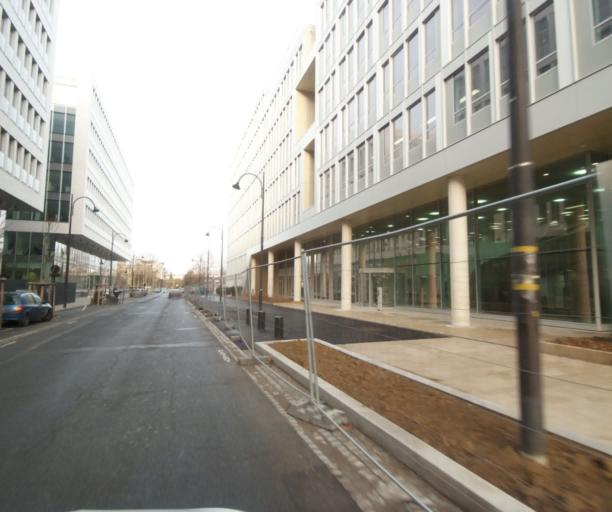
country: FR
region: Ile-de-France
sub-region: Departement des Yvelines
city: Chatou
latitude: 48.8921
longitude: 2.1740
